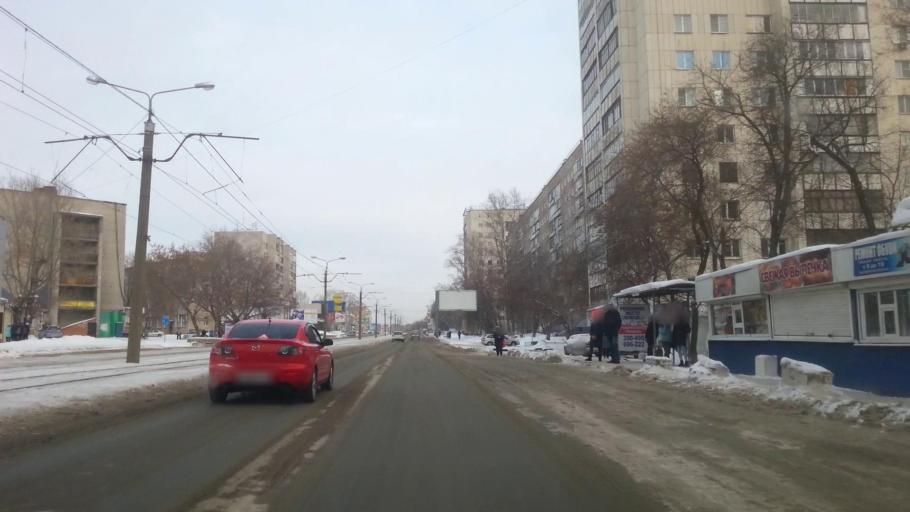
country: RU
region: Altai Krai
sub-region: Gorod Barnaulskiy
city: Barnaul
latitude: 53.3707
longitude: 83.7432
